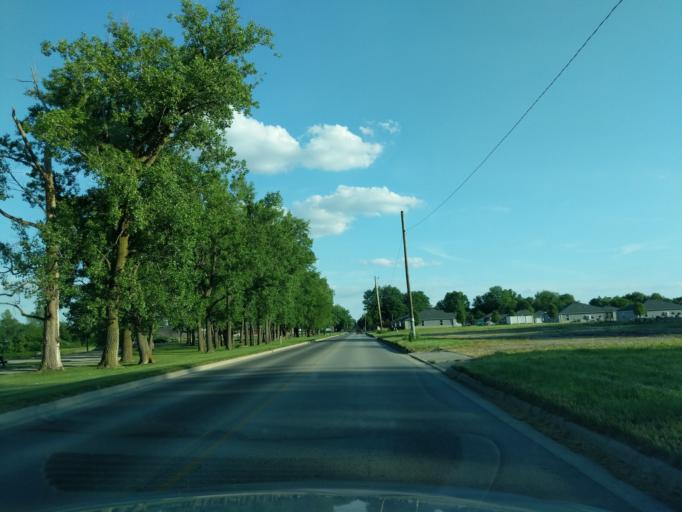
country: US
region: Indiana
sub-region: Huntington County
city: Huntington
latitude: 40.8929
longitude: -85.4713
